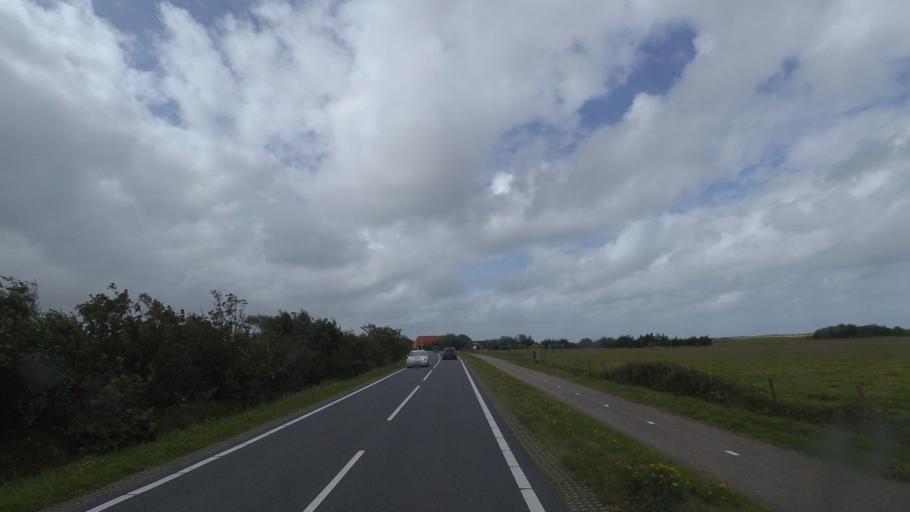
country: NL
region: Friesland
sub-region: Gemeente Ameland
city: Hollum
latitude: 53.4469
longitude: 5.6728
